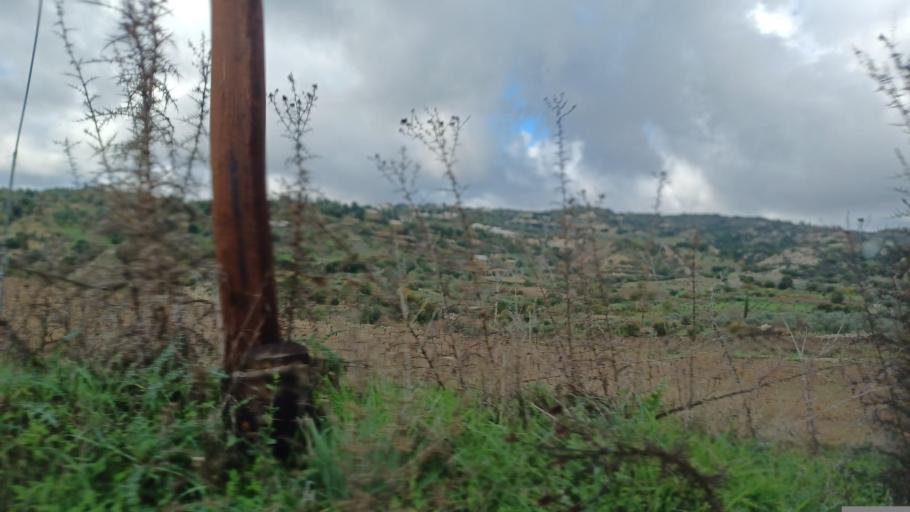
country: CY
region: Pafos
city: Mesogi
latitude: 34.8481
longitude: 32.5141
